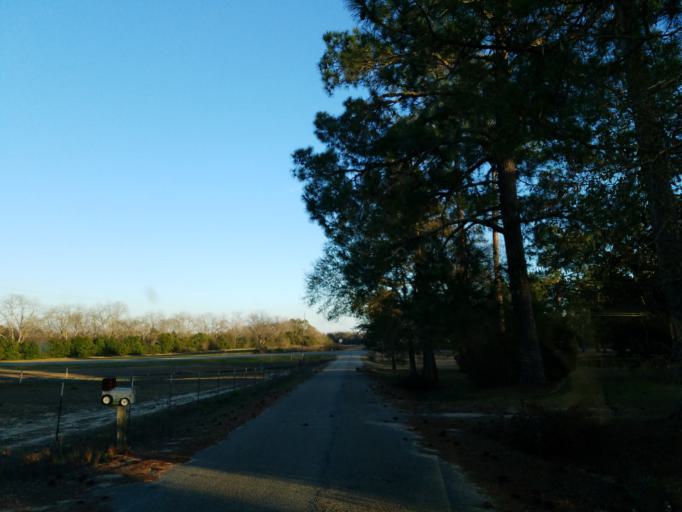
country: US
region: Georgia
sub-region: Worth County
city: Sylvester
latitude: 31.5832
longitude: -83.7847
